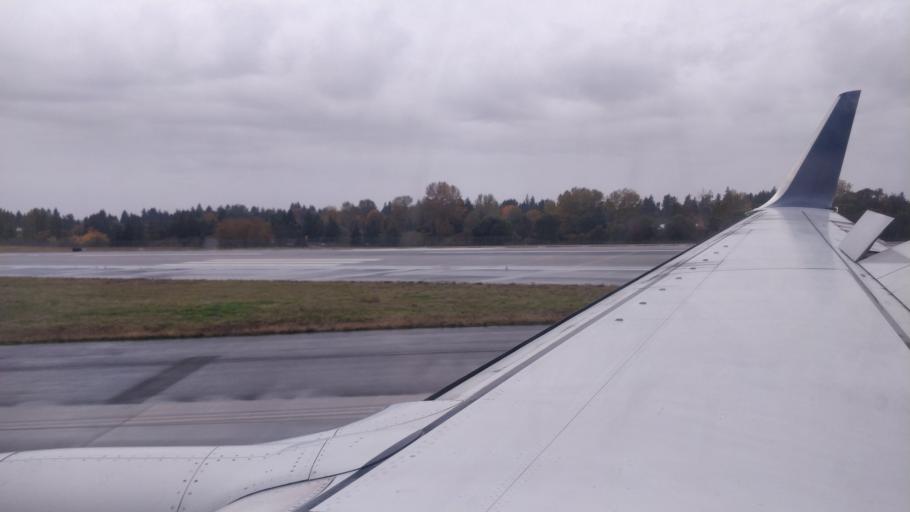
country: US
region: Washington
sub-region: King County
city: Normandy Park
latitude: 47.4426
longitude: -122.3170
